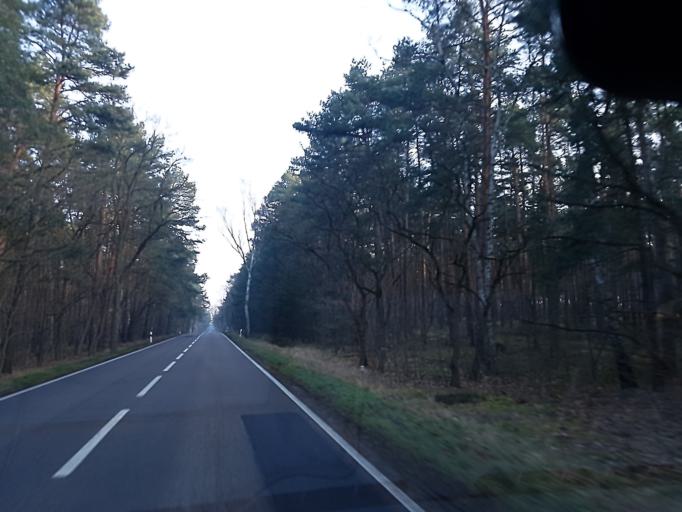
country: DE
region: Brandenburg
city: Graben
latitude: 52.2525
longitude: 12.4389
